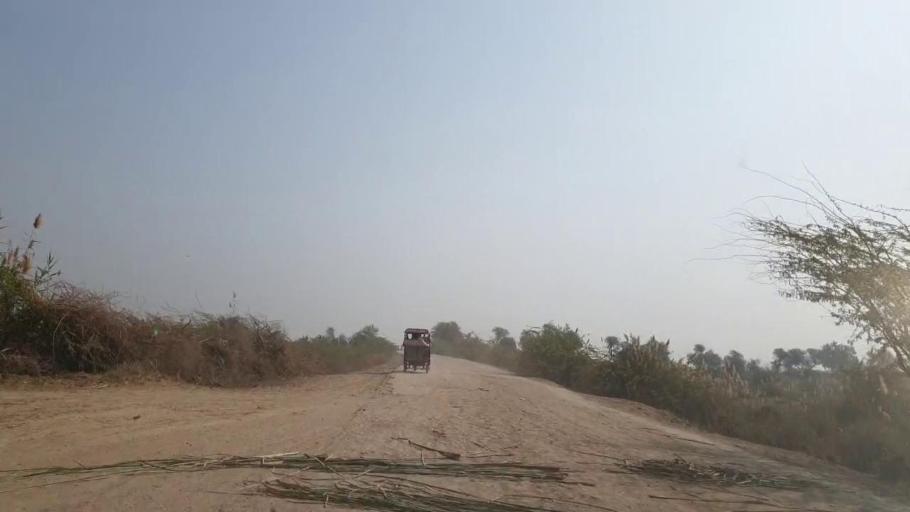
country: PK
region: Sindh
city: Mirpur Khas
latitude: 25.5561
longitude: 69.0941
